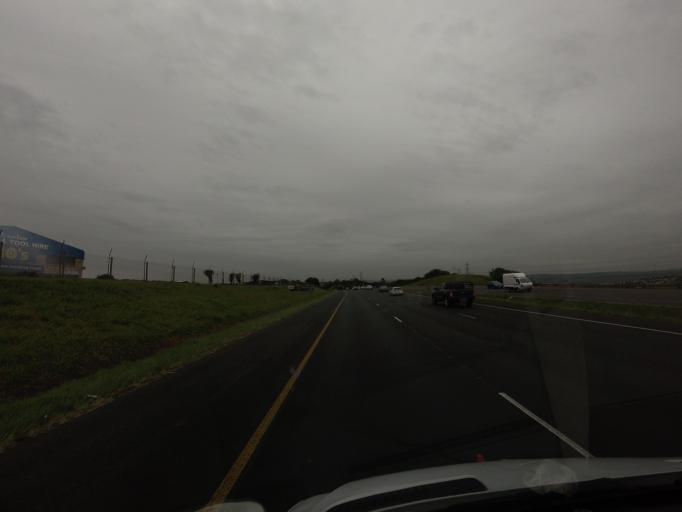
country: ZA
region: KwaZulu-Natal
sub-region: eThekwini Metropolitan Municipality
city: Durban
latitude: -29.7490
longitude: 31.0307
